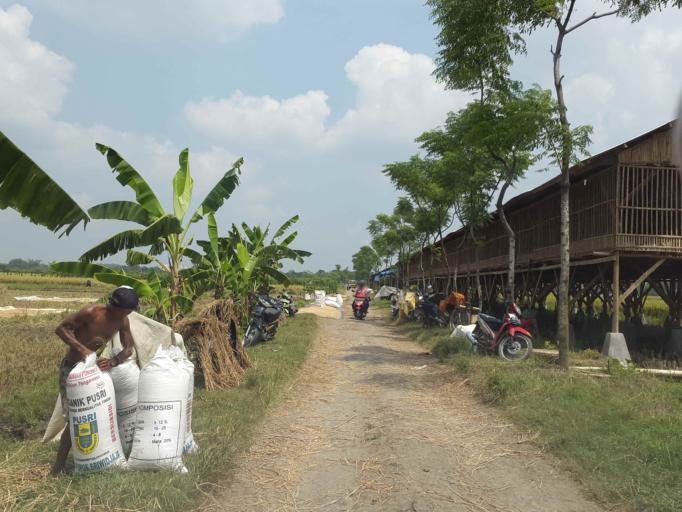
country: ID
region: Central Java
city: Dukuhkopi
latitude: -6.9566
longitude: 108.8095
